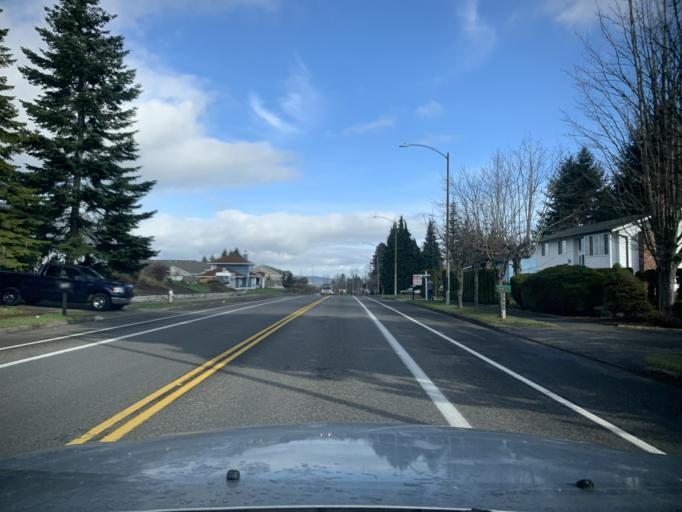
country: US
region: Washington
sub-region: Pierce County
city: Fircrest
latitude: 47.2786
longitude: -122.5226
